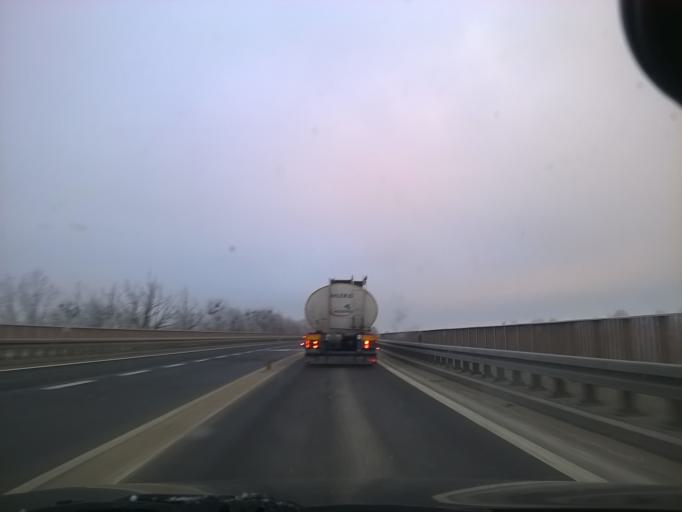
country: PL
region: Warmian-Masurian Voivodeship
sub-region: Powiat mragowski
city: Mragowo
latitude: 53.8642
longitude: 21.2766
